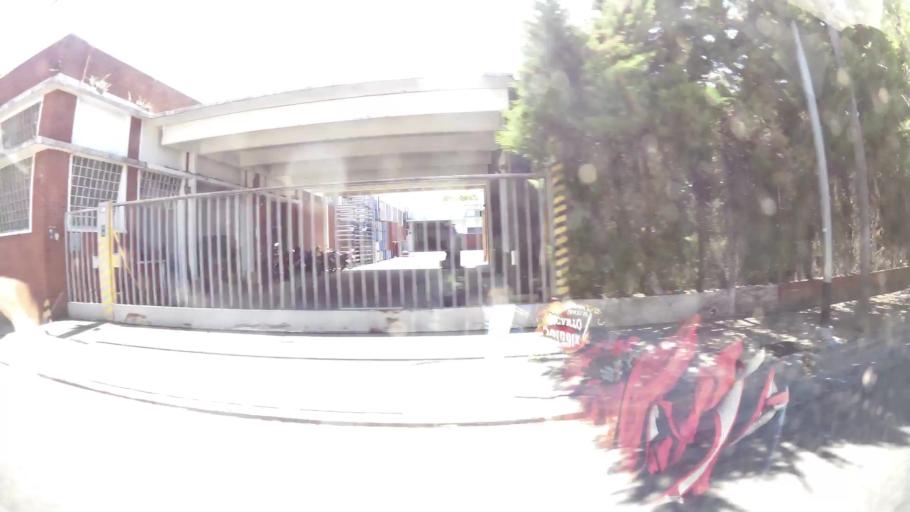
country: AR
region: Buenos Aires
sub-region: Partido de General San Martin
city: General San Martin
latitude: -34.5415
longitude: -58.5378
